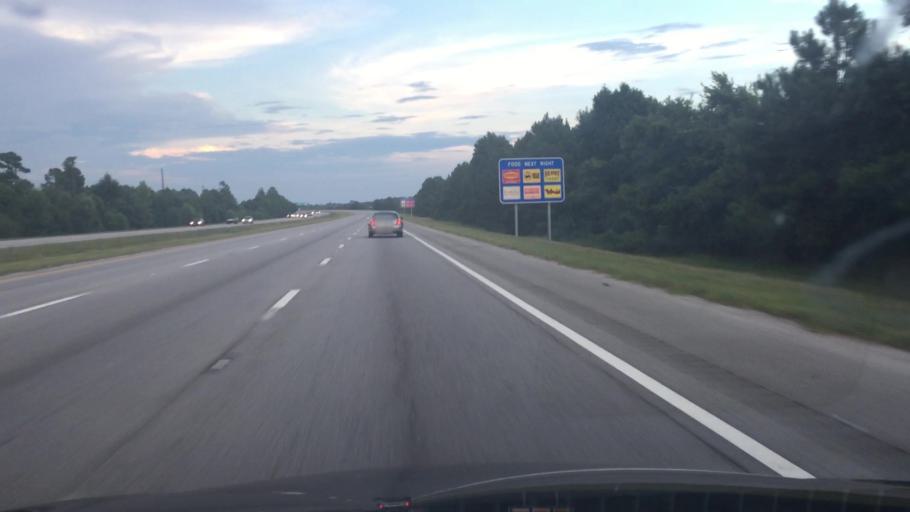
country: US
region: South Carolina
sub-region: Horry County
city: North Myrtle Beach
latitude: 33.8339
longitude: -78.7128
